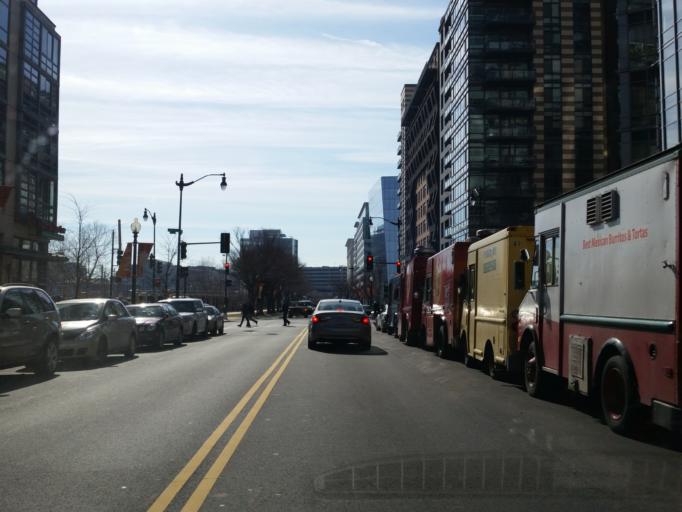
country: US
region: Washington, D.C.
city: Washington, D.C.
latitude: 38.9062
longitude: -77.0059
